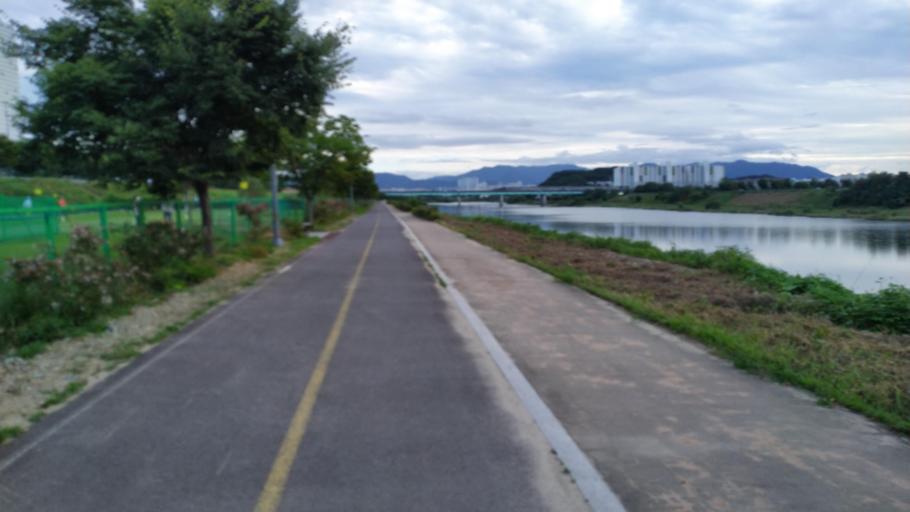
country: KR
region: Daegu
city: Daegu
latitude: 35.9246
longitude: 128.6325
